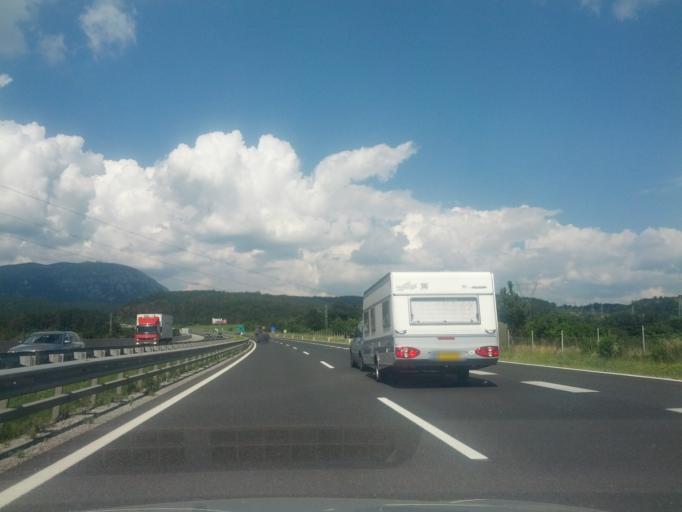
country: SI
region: Divaca
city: Divaca
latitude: 45.7232
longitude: 14.0118
